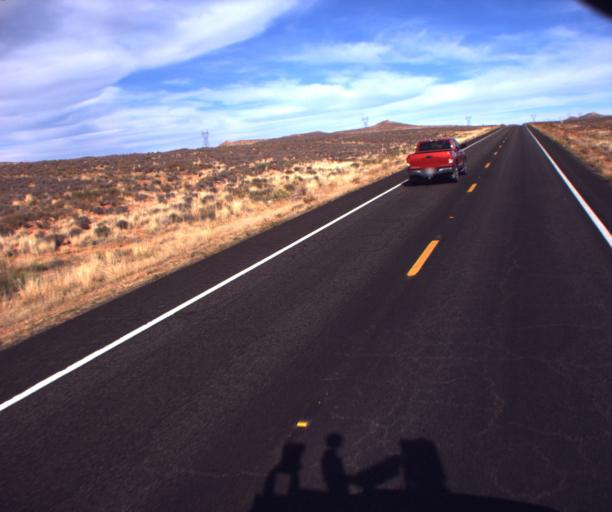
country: US
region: Arizona
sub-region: Apache County
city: Many Farms
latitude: 36.9378
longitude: -109.5540
